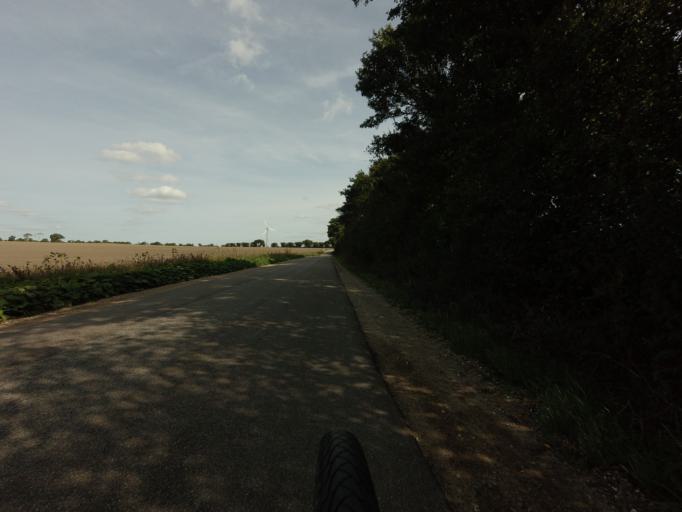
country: DK
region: Zealand
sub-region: Faxe Kommune
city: Fakse
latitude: 55.1916
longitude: 12.1108
